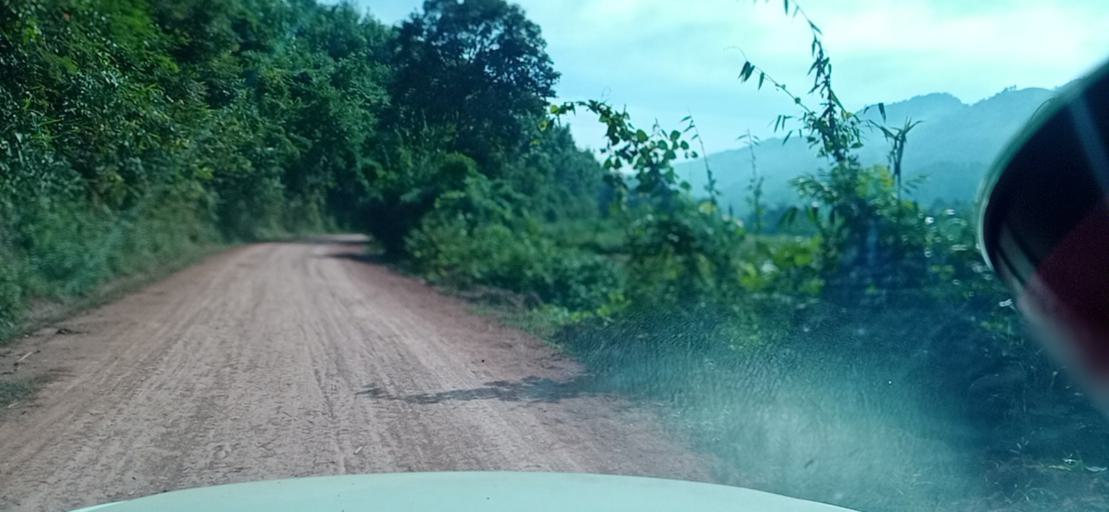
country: TH
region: Changwat Bueng Kan
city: Pak Khat
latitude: 18.6703
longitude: 103.1949
